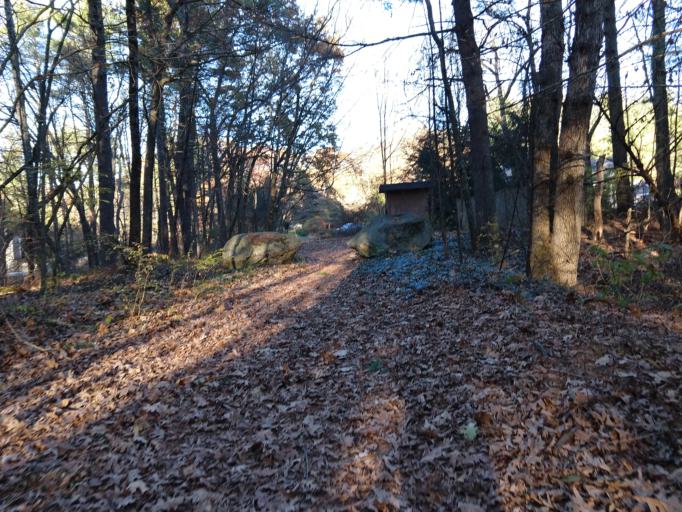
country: US
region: Massachusetts
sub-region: Middlesex County
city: Westford
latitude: 42.5380
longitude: -71.4182
